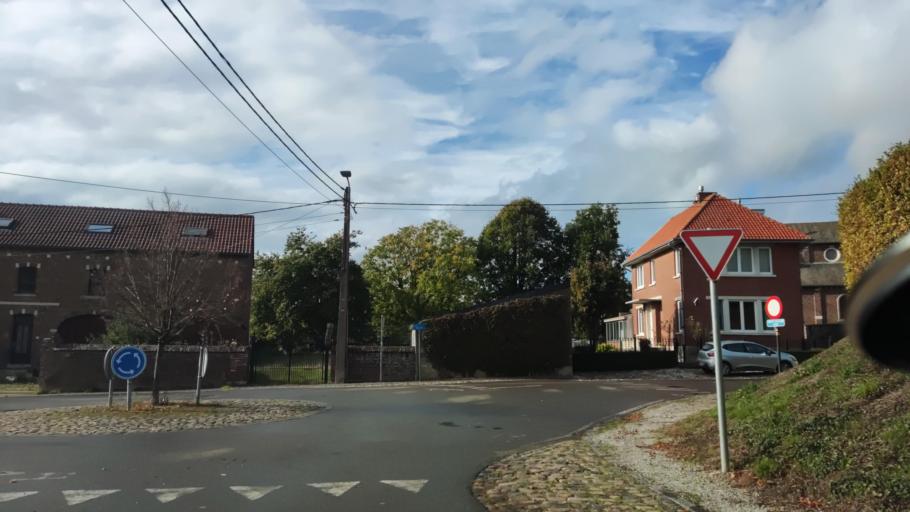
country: BE
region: Wallonia
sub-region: Province du Brabant Wallon
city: Jodoigne
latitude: 50.7442
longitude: 4.8749
